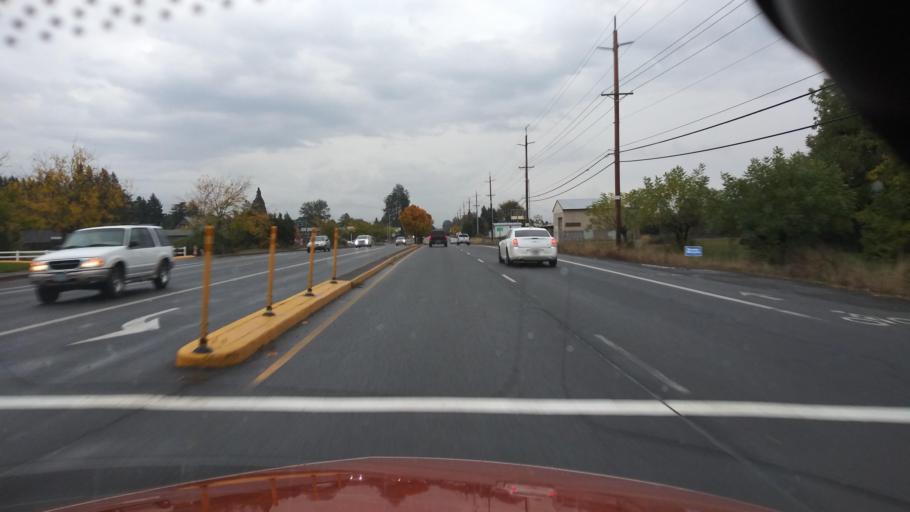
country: US
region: Oregon
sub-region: Washington County
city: Cornelius
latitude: 45.5200
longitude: -123.0397
